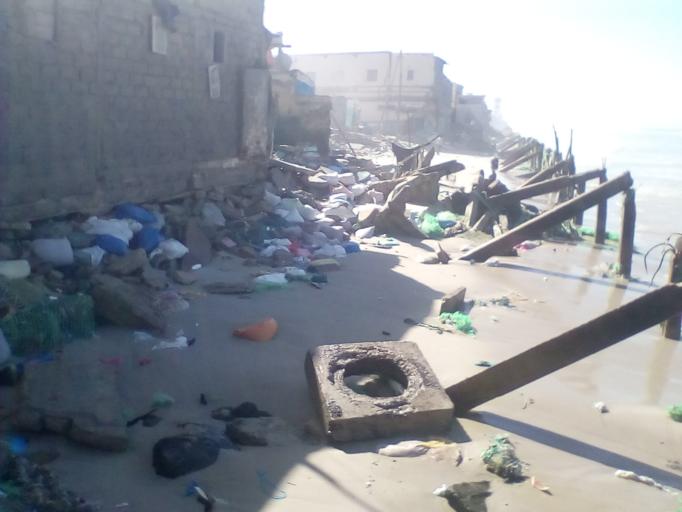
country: SN
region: Saint-Louis
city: Saint-Louis
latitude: 16.0211
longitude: -16.5094
